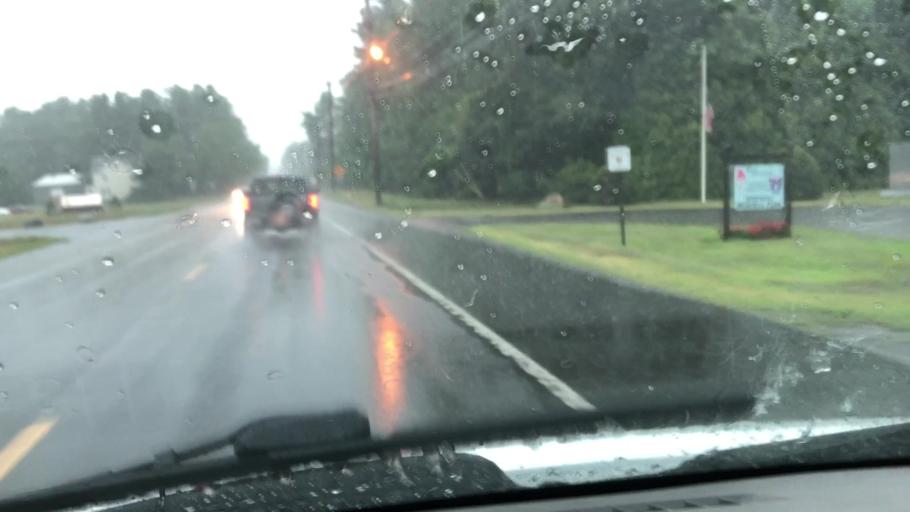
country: US
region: Massachusetts
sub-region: Hampden County
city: Westfield
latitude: 42.1636
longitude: -72.7263
